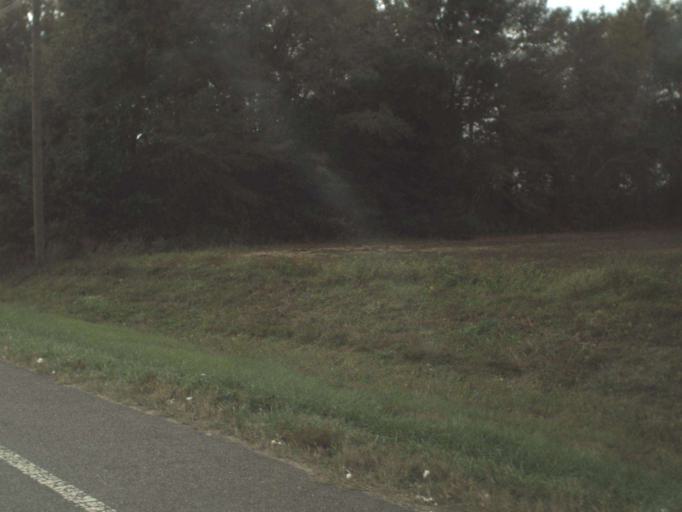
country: US
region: Florida
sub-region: Santa Rosa County
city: Point Baker
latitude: 30.7870
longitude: -87.0925
